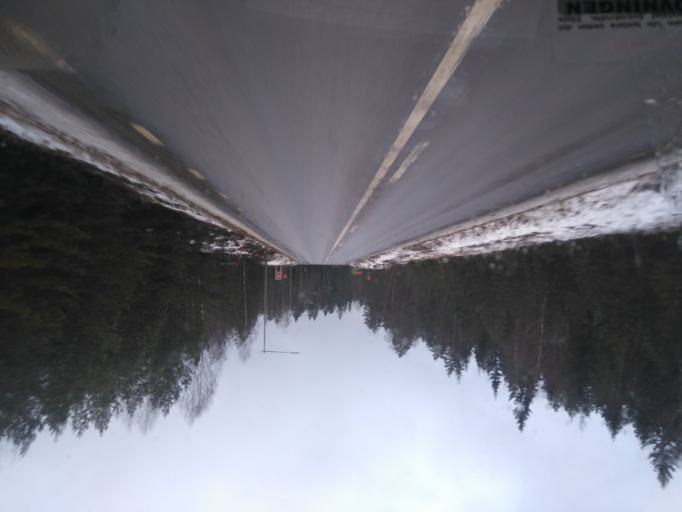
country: SE
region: Joenkoeping
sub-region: Eksjo Kommun
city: Mariannelund
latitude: 57.6217
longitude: 15.5934
